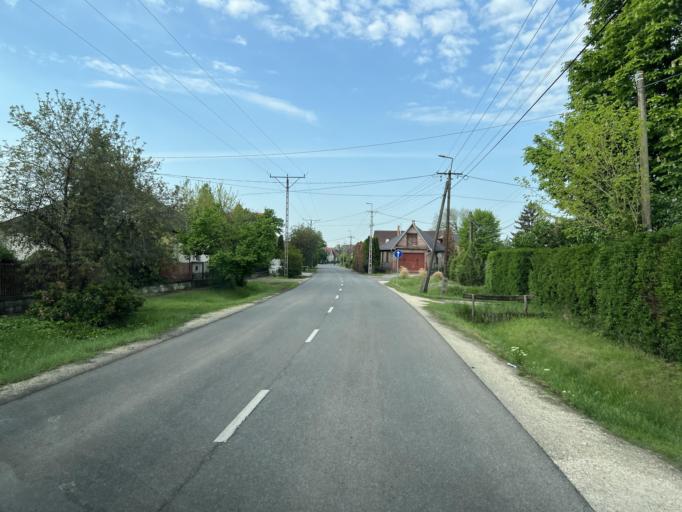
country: HU
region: Pest
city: Abony
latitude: 47.1932
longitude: 20.0109
